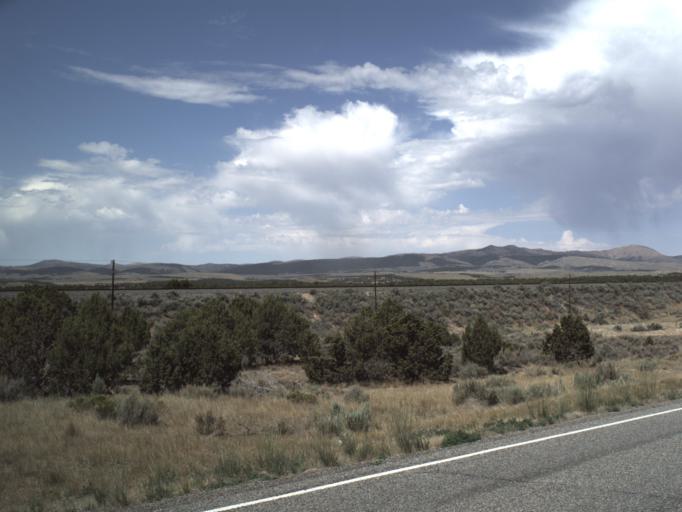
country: US
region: Utah
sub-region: Utah County
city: Genola
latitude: 39.9351
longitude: -112.1755
